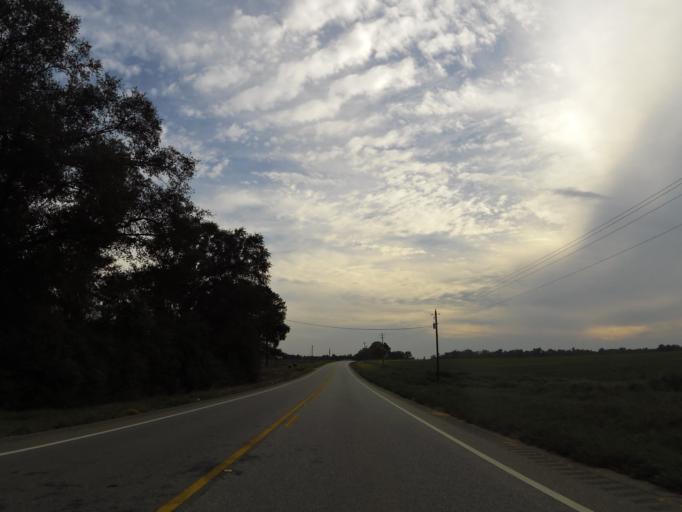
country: US
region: Alabama
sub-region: Monroe County
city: Frisco City
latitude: 31.3331
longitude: -87.4569
